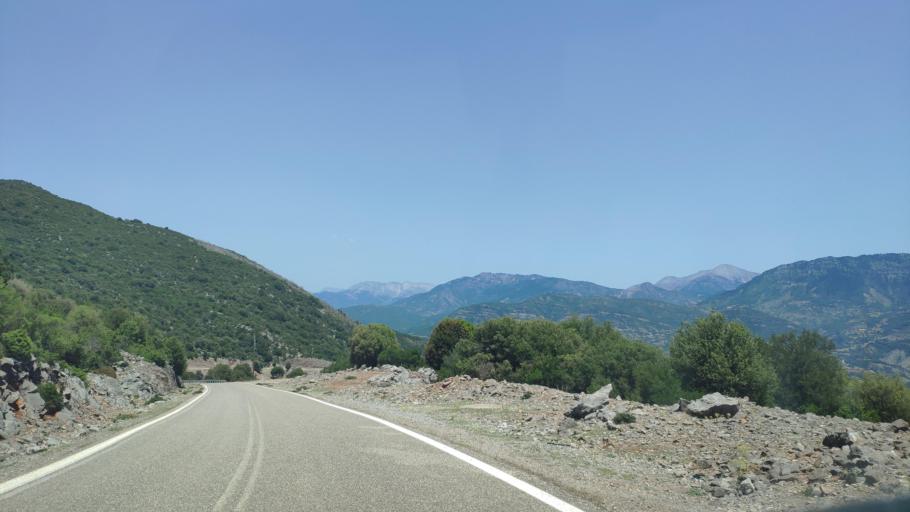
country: GR
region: Central Greece
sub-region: Nomos Evrytanias
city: Kerasochori
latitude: 39.0871
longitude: 21.4139
